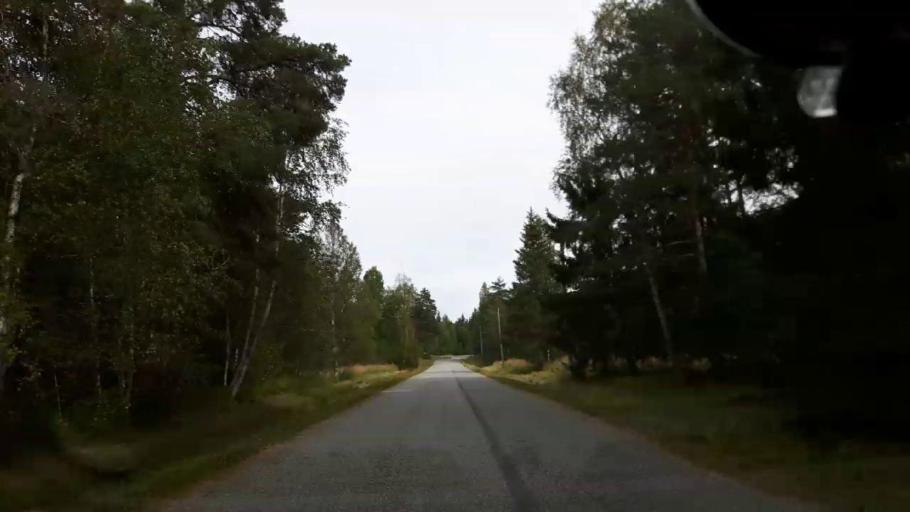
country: SE
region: Jaemtland
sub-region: Ragunda Kommun
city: Hammarstrand
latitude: 63.0098
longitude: 16.0959
